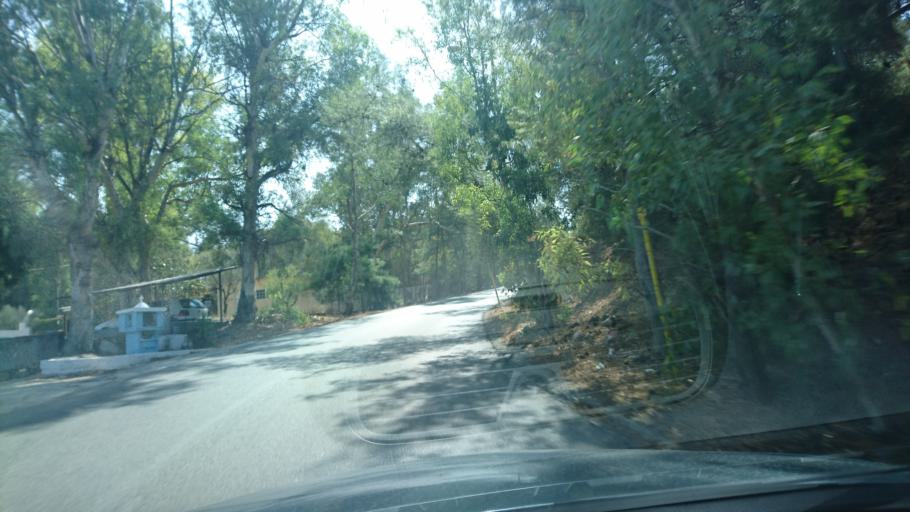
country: GR
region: Attica
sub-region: Nomarchia Athinas
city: Kaisariani
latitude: 37.9640
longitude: 23.7765
